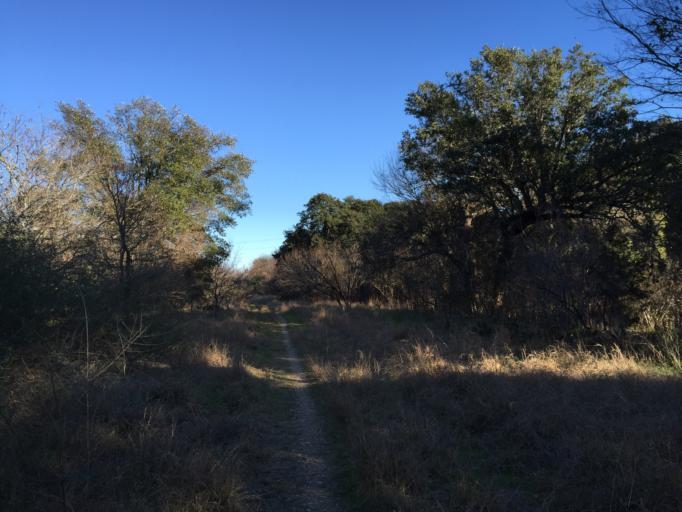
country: US
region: Texas
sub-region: Bexar County
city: Castle Hills
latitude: 29.5578
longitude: -98.5006
